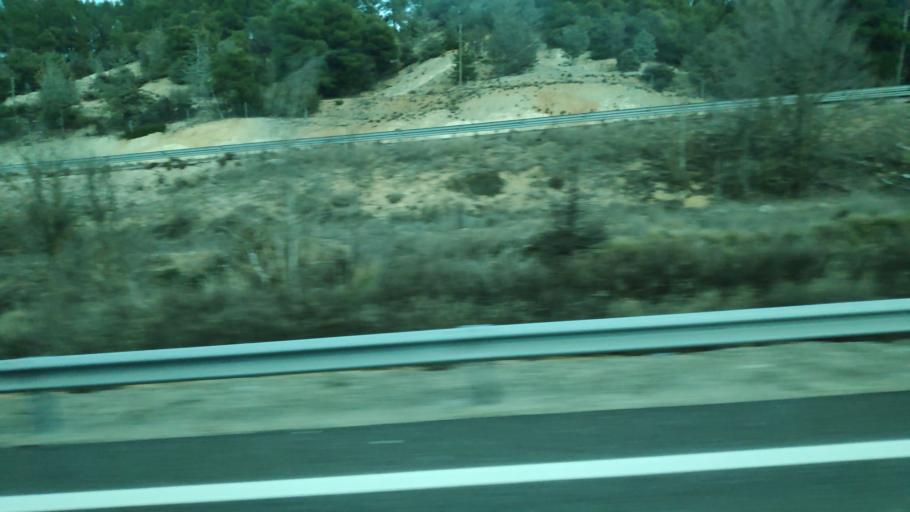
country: ES
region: Castille-La Mancha
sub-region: Provincia de Cuenca
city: Tarancon
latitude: 40.0200
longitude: -3.0341
